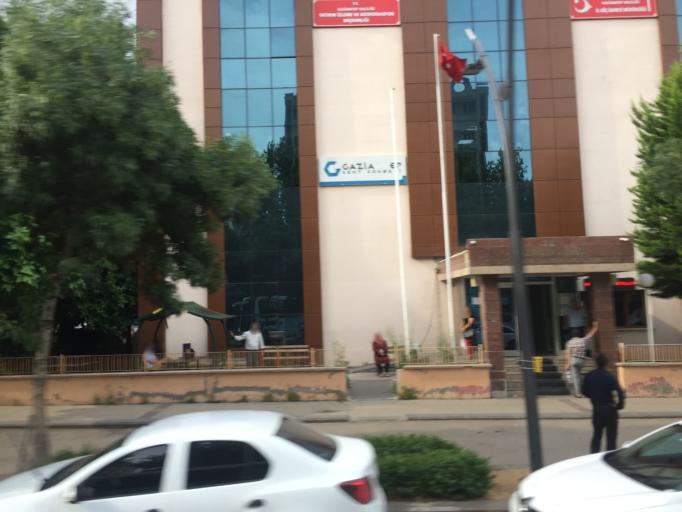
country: TR
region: Gaziantep
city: Gaziantep
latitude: 37.0672
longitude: 37.3724
